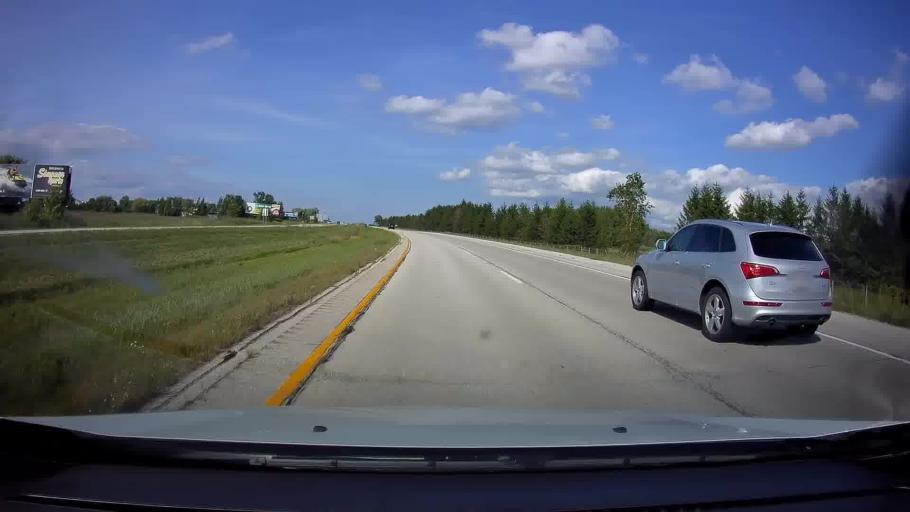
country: US
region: Wisconsin
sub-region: Brown County
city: Bellevue
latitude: 44.5281
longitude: -87.8849
